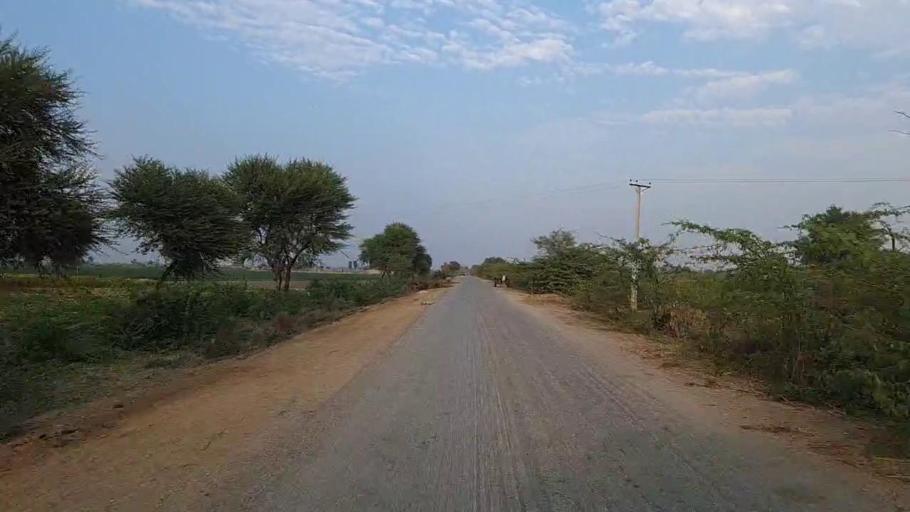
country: PK
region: Sindh
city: Samaro
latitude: 25.3962
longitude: 69.3771
